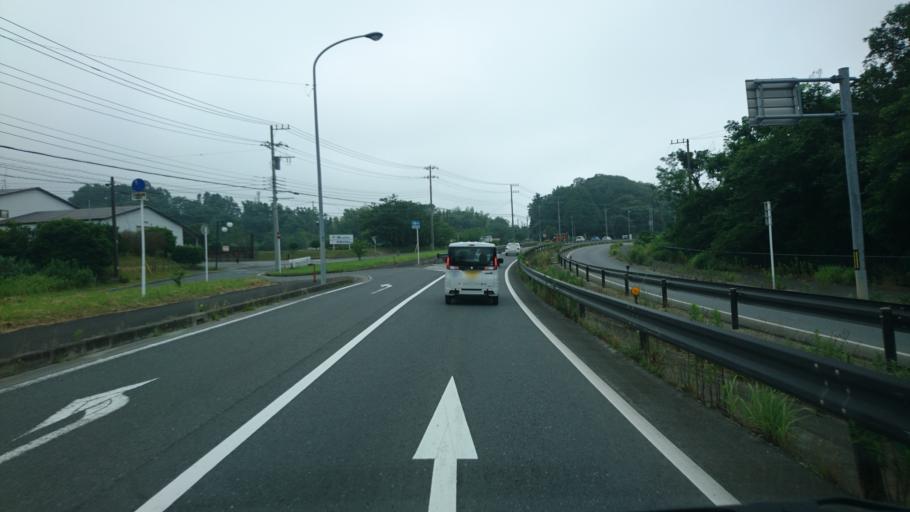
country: JP
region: Chiba
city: Kimitsu
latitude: 35.2493
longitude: 139.8871
